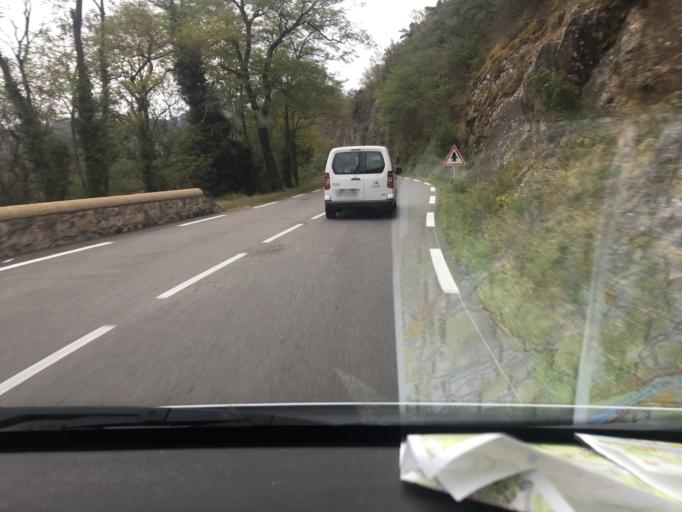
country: FR
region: Rhone-Alpes
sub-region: Departement de l'Ardeche
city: Saint-Jean-de-Muzols
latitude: 45.0657
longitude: 4.7569
